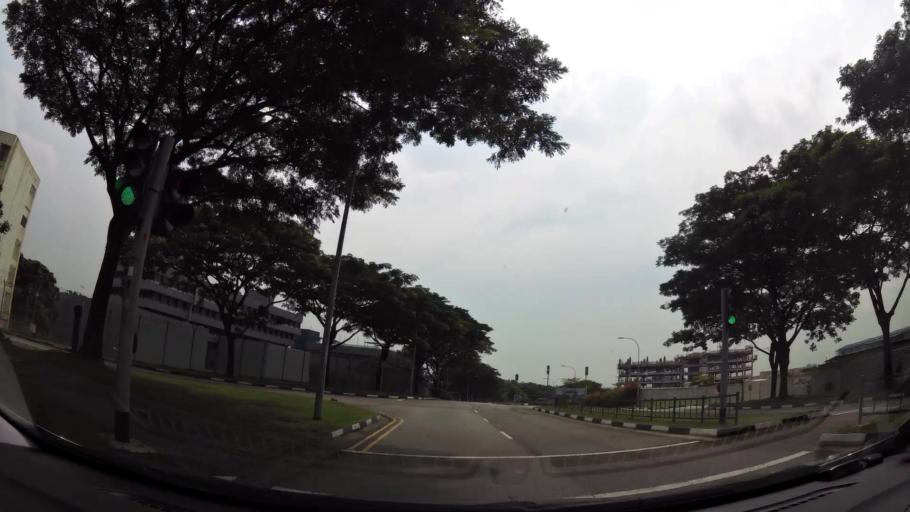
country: SG
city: Singapore
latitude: 1.3458
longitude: 103.8989
